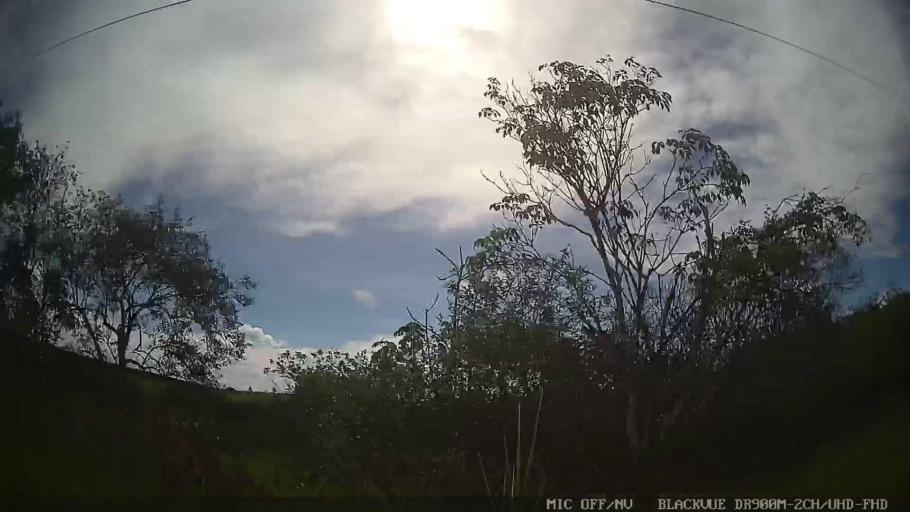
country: BR
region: Sao Paulo
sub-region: Conchas
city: Conchas
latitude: -22.9527
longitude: -47.9836
